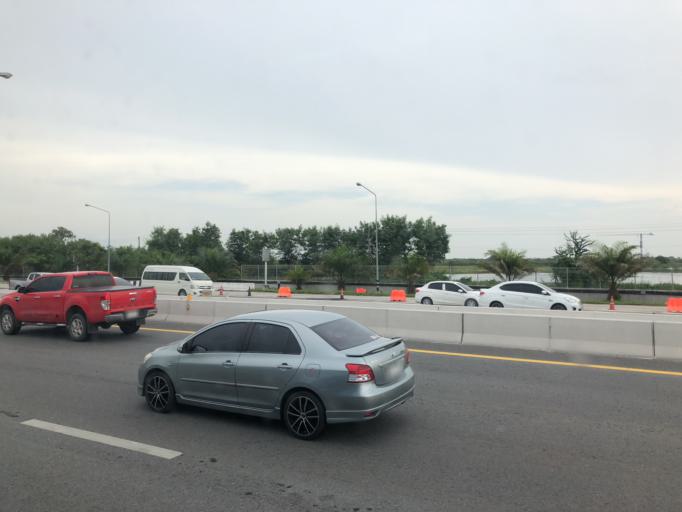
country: TH
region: Chachoengsao
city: Bang Pakong
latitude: 13.5036
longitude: 101.0393
